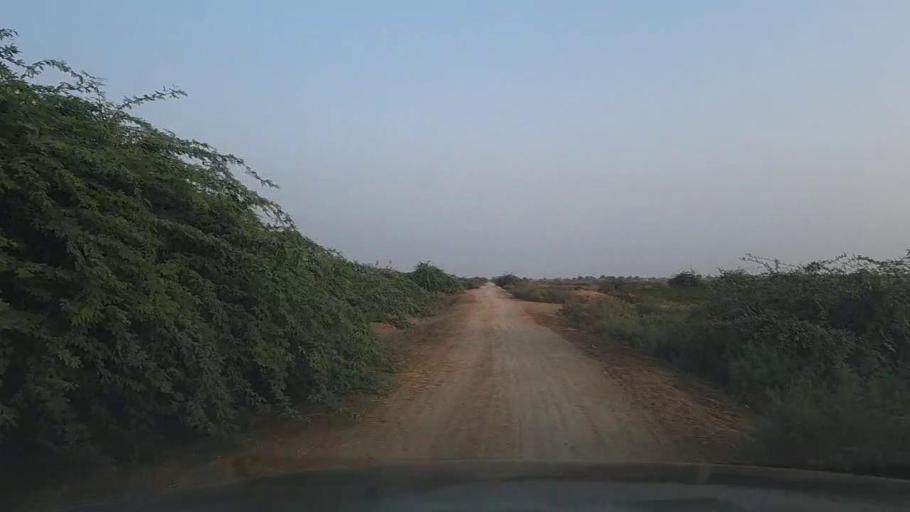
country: PK
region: Sindh
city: Mirpur Batoro
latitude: 24.5441
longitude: 68.3932
